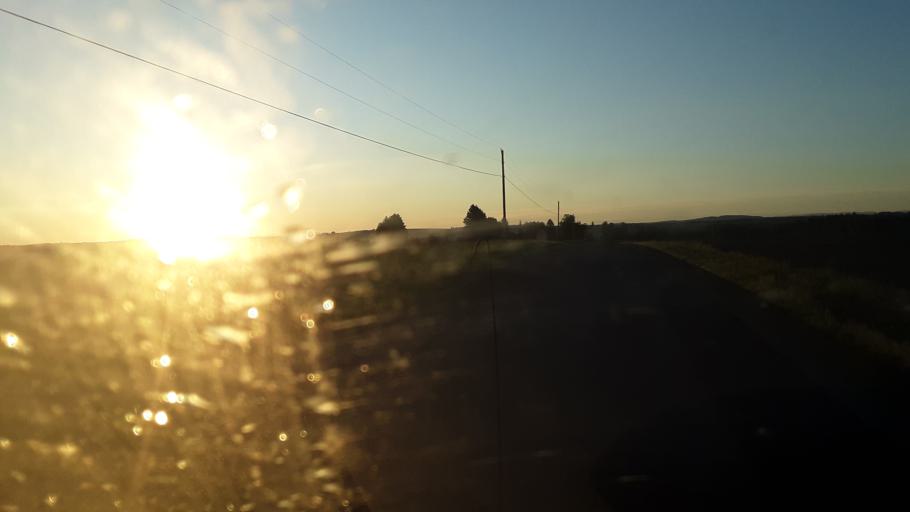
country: US
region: Maine
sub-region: Aroostook County
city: Caribou
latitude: 46.8028
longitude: -68.1037
